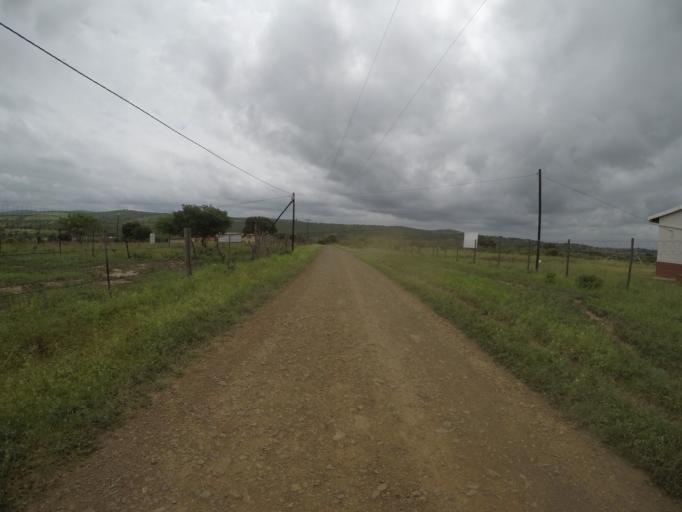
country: ZA
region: KwaZulu-Natal
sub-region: uThungulu District Municipality
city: Empangeni
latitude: -28.5985
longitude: 31.8320
